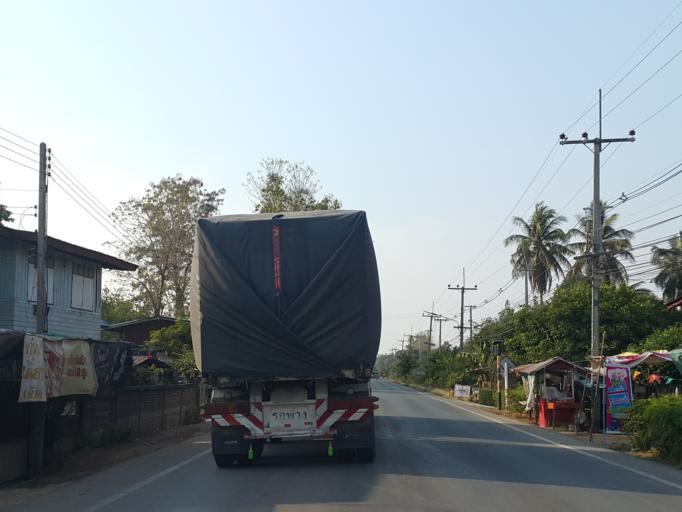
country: TH
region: Phitsanulok
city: Phrom Phiram
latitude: 17.0485
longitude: 100.1861
